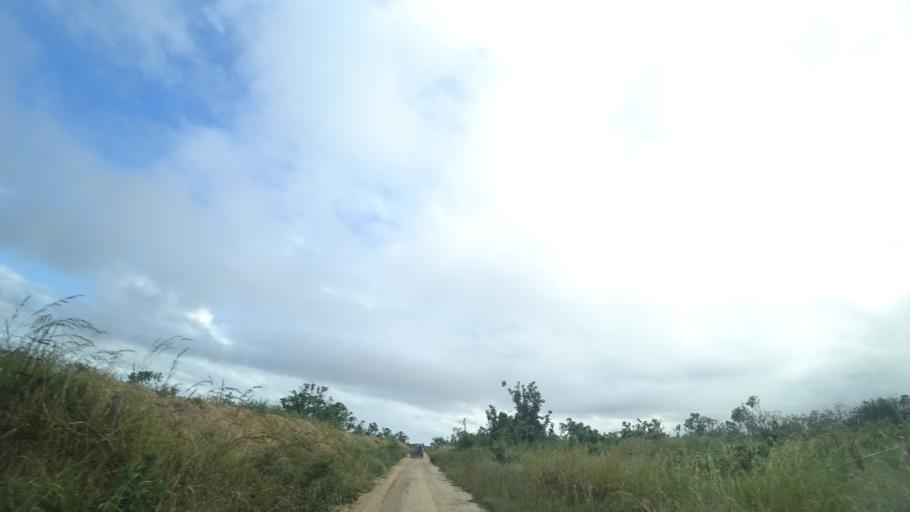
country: MZ
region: Sofala
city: Beira
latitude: -19.6205
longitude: 35.0606
